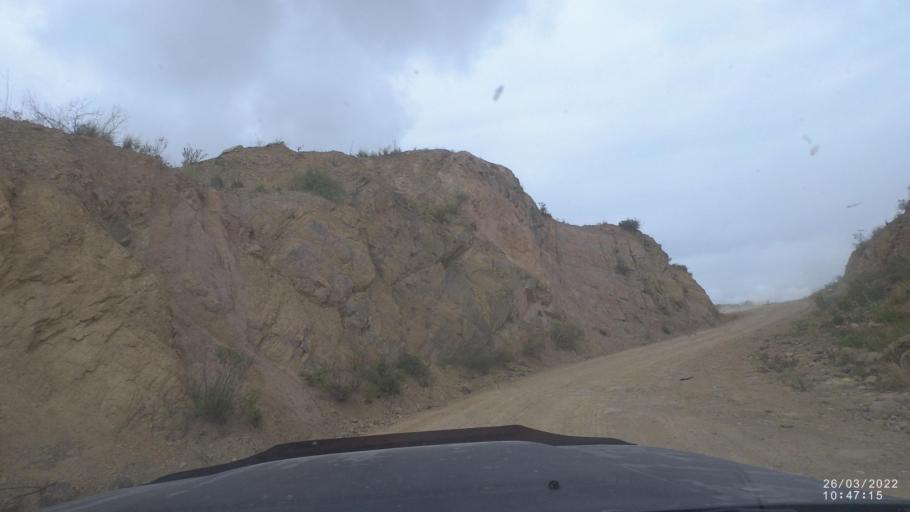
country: BO
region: Cochabamba
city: Tarata
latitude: -17.4914
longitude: -66.0478
